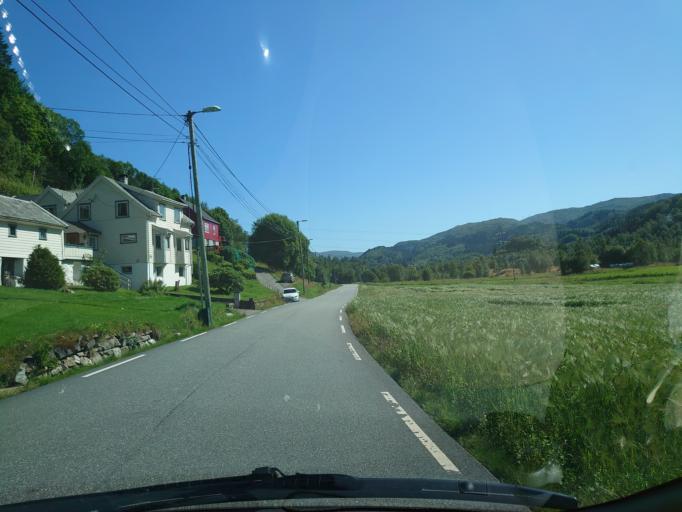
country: NO
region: Hordaland
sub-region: Bergen
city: Ytre Arna
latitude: 60.4635
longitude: 5.3853
